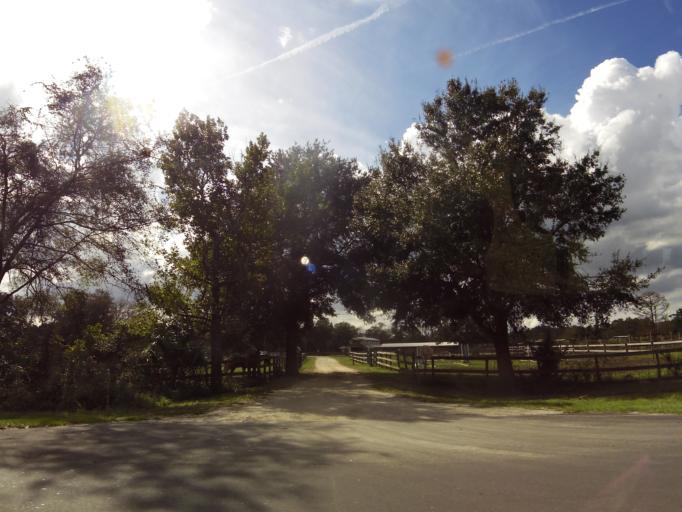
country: US
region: Florida
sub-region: Saint Johns County
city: Villano Beach
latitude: 29.9984
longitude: -81.3958
